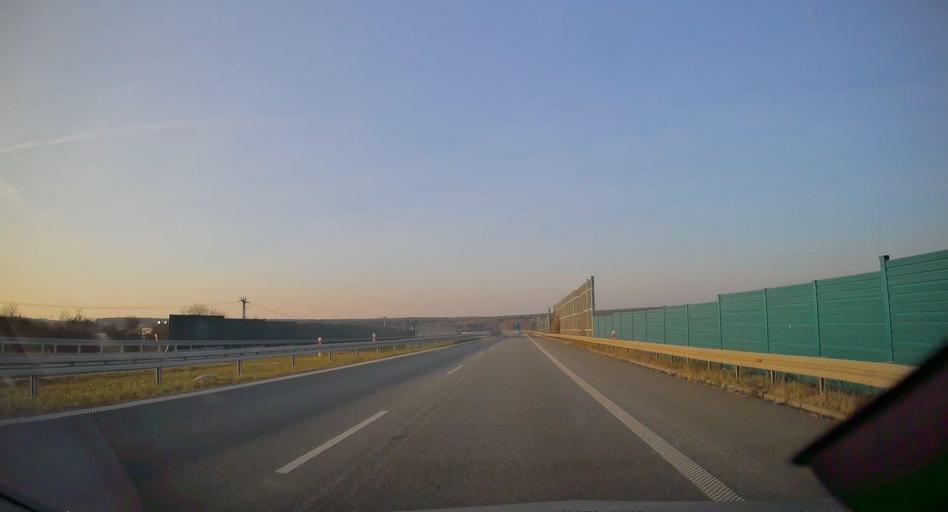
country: PL
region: Silesian Voivodeship
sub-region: Powiat bedzinski
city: Mierzecice
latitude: 50.4455
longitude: 19.1394
